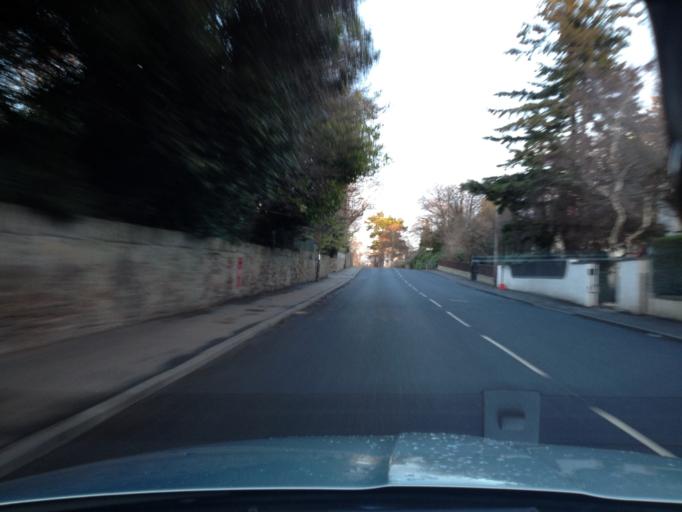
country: GB
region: Scotland
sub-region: Edinburgh
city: Colinton
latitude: 55.9045
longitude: -3.2611
